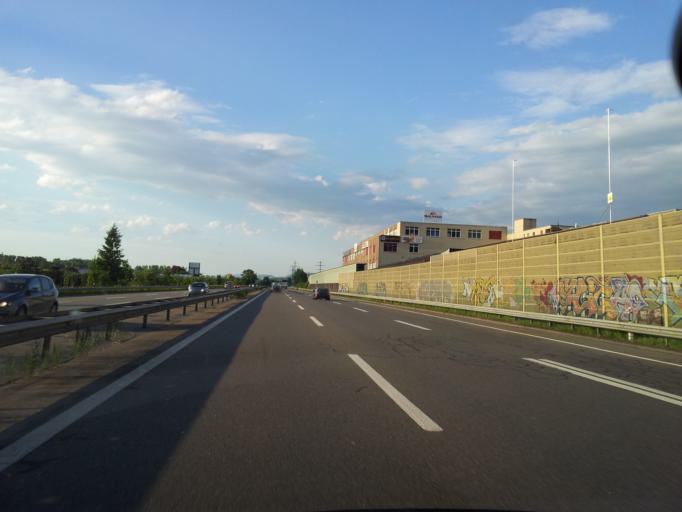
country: CH
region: Lucerne
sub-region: Lucerne-Land District
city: Root
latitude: 47.1253
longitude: 8.3945
